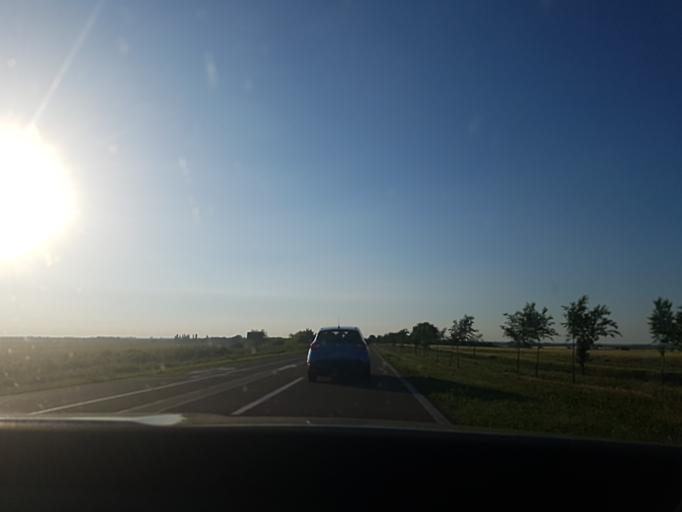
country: RO
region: Timis
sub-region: Comuna Moravita
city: Moravita
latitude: 45.2190
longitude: 21.2980
